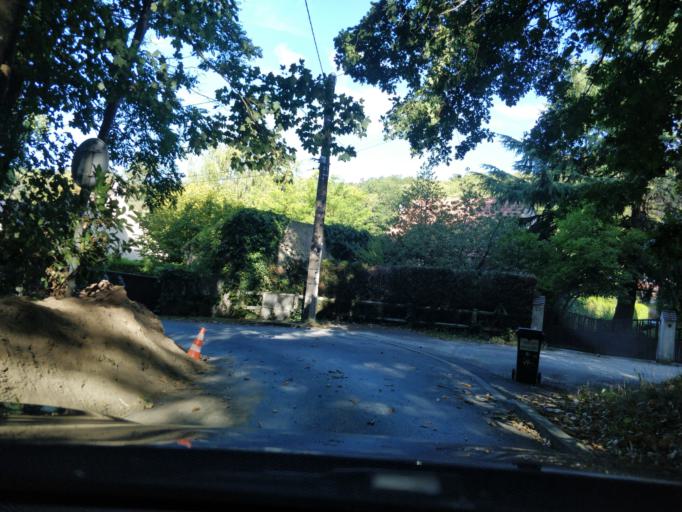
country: FR
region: Ile-de-France
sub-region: Departement de l'Essonne
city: Forges-les-Bains
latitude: 48.6326
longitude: 2.0977
